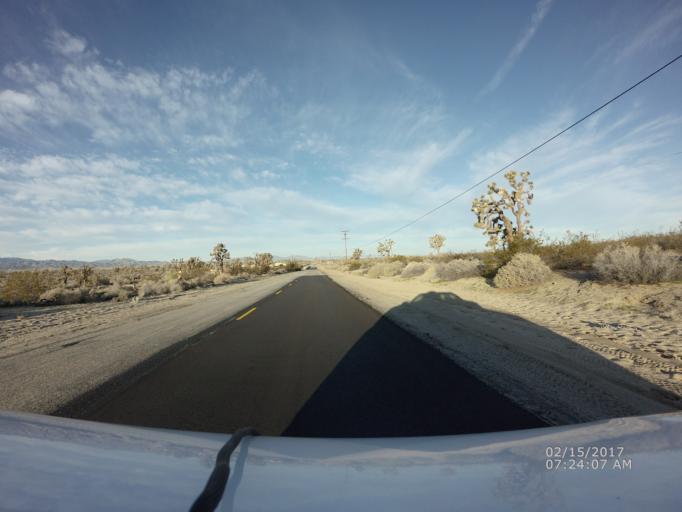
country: US
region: California
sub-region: Los Angeles County
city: Lake Los Angeles
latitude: 34.5877
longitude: -117.8654
